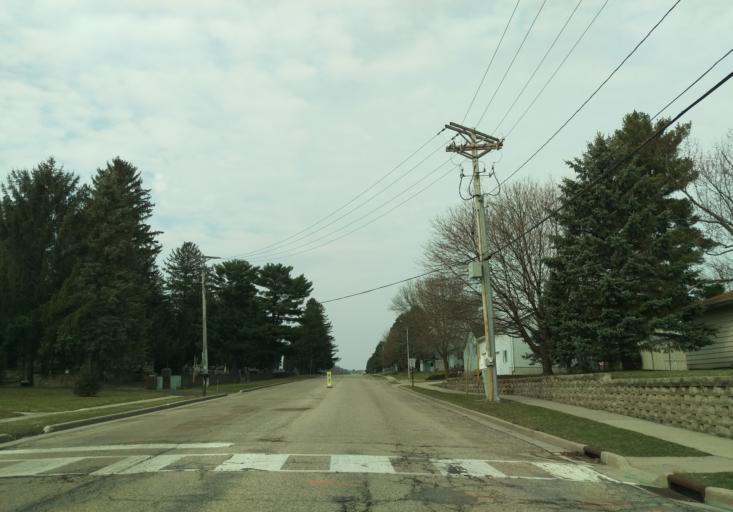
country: US
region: Wisconsin
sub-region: Columbia County
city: Lodi
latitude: 43.3125
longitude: -89.5361
